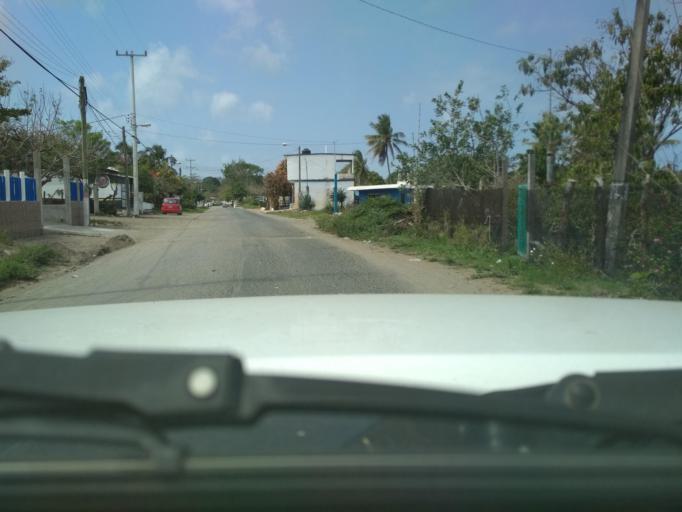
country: MX
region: Veracruz
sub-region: Veracruz
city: Delfino Victoria (Santa Fe)
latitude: 19.2537
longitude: -96.2637
